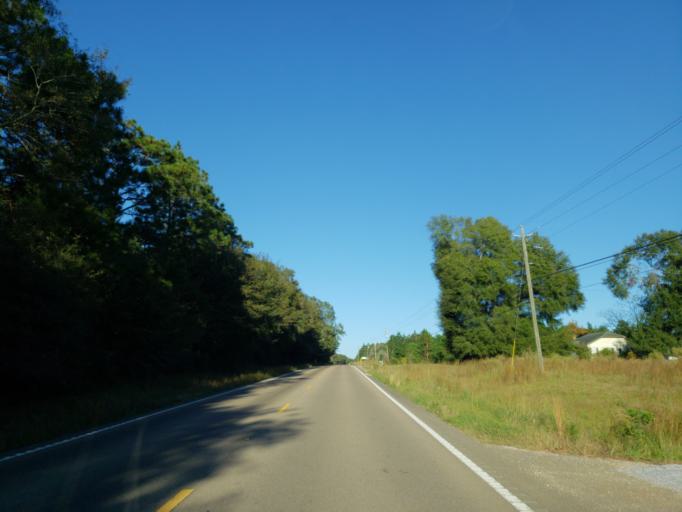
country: US
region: Mississippi
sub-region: Perry County
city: Richton
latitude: 31.3706
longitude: -88.8703
